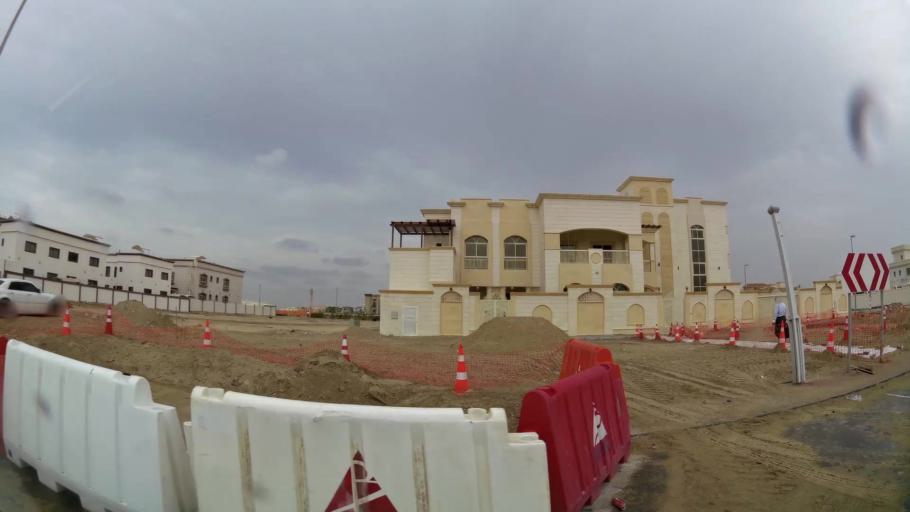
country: AE
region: Abu Dhabi
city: Abu Dhabi
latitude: 24.3577
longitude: 54.6260
